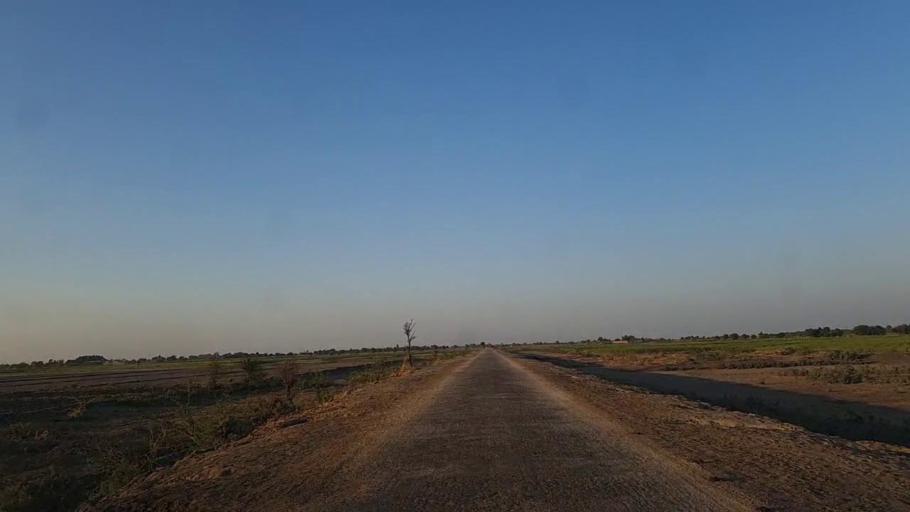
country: PK
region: Sindh
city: Naukot
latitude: 25.0206
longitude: 69.4167
